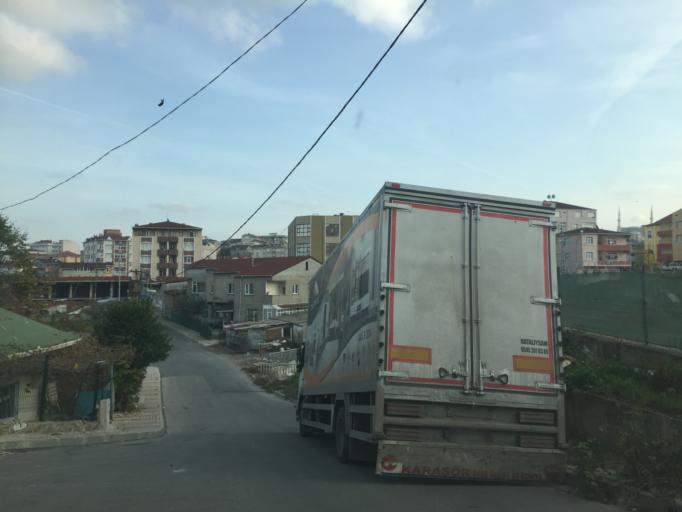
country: TR
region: Istanbul
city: Sultanbeyli
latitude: 40.9473
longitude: 29.2968
